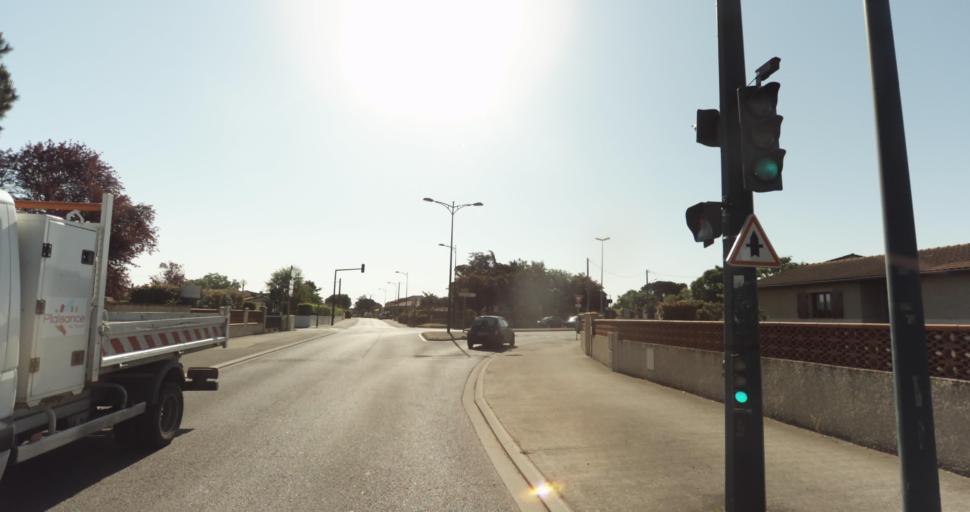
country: FR
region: Midi-Pyrenees
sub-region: Departement de la Haute-Garonne
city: Plaisance-du-Touch
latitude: 43.5605
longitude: 1.3004
